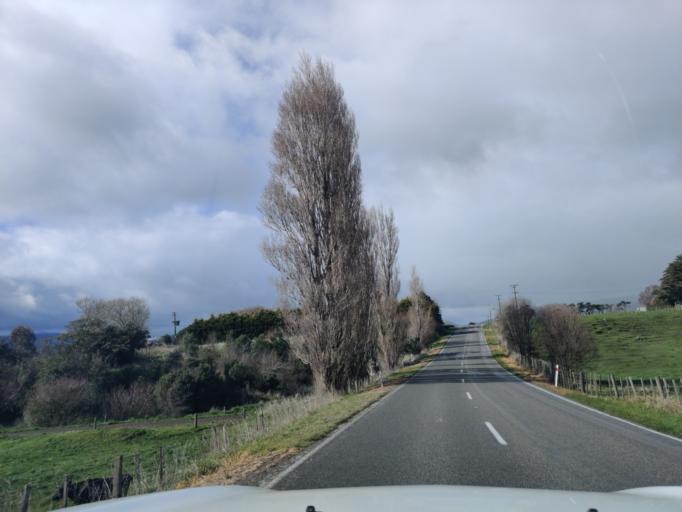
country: NZ
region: Manawatu-Wanganui
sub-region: Palmerston North City
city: Palmerston North
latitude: -40.2912
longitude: 175.7268
